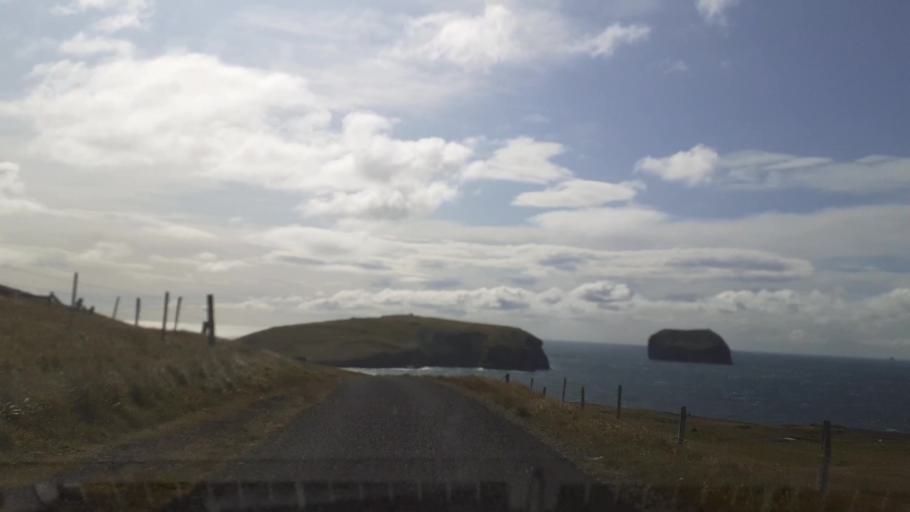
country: IS
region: South
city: Vestmannaeyjar
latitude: 63.4184
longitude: -20.2813
